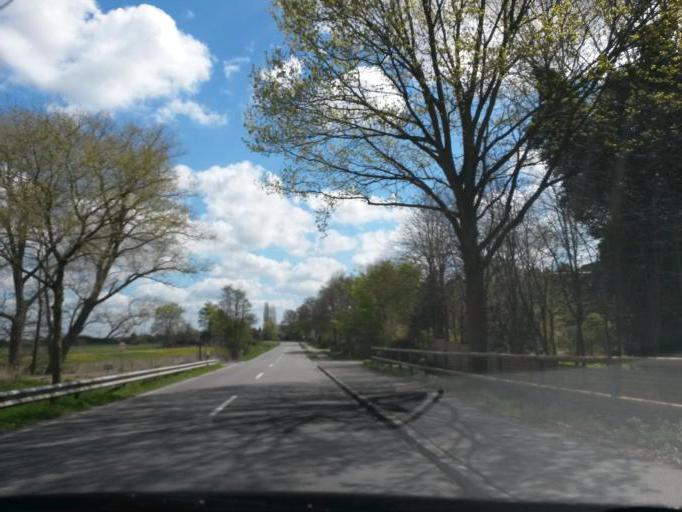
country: DE
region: Schleswig-Holstein
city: Neuendeich
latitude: 53.6751
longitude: 9.6113
